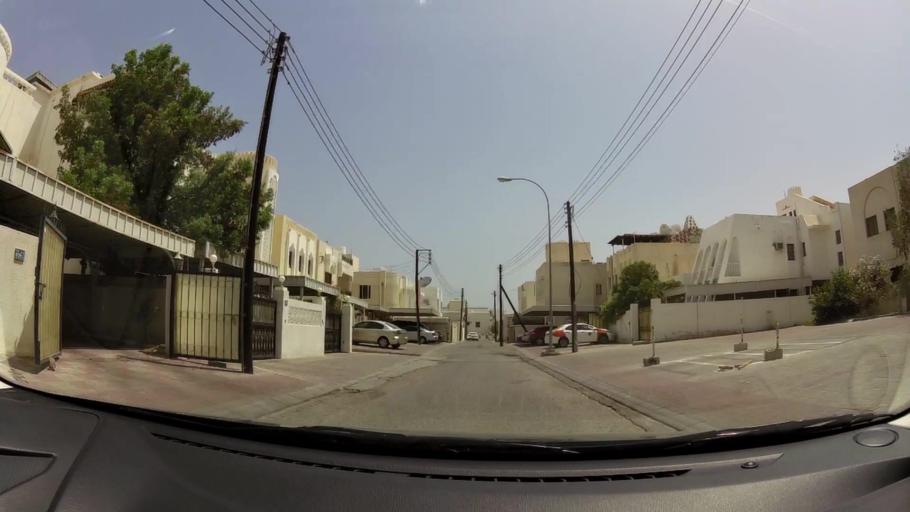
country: OM
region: Muhafazat Masqat
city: Bawshar
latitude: 23.5907
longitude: 58.4344
